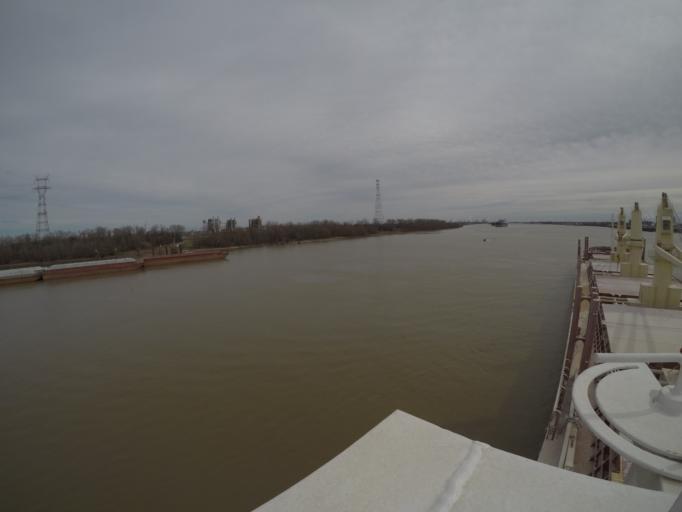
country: US
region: Louisiana
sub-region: Saint Charles Parish
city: Montz
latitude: 29.9995
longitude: -90.4681
